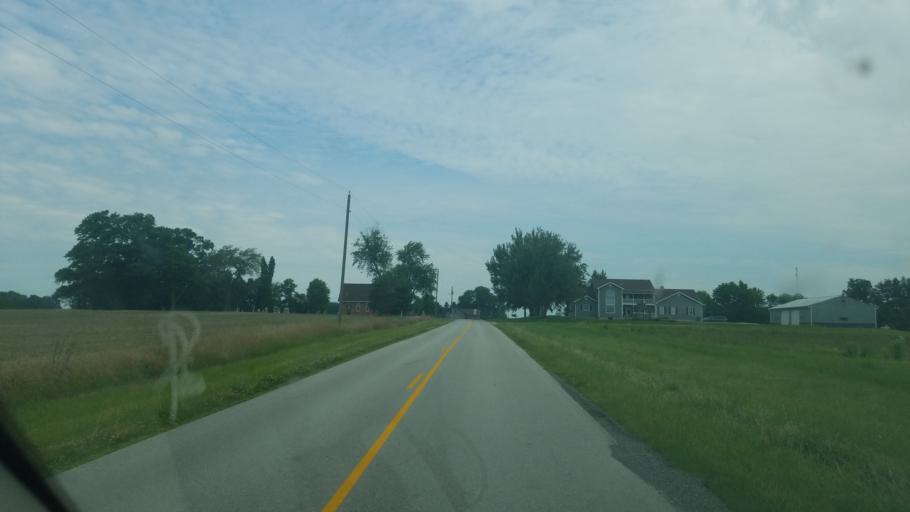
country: US
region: Ohio
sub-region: Wyandot County
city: Carey
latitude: 41.0340
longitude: -83.4399
